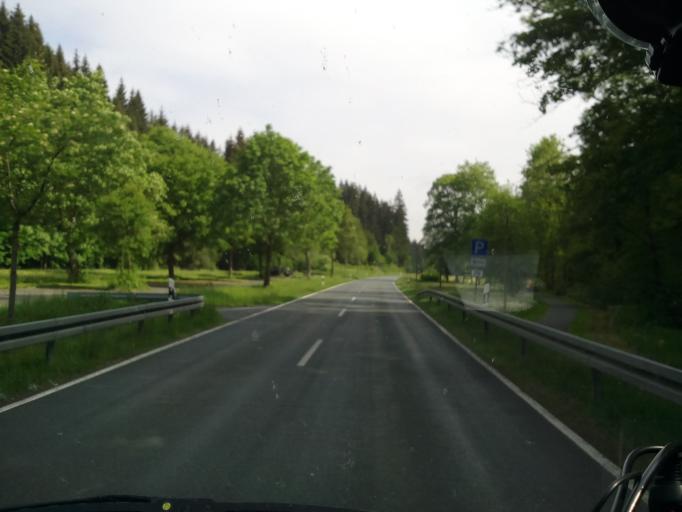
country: DE
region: Bavaria
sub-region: Upper Franconia
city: Steinwiesen
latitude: 50.2977
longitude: 11.4455
